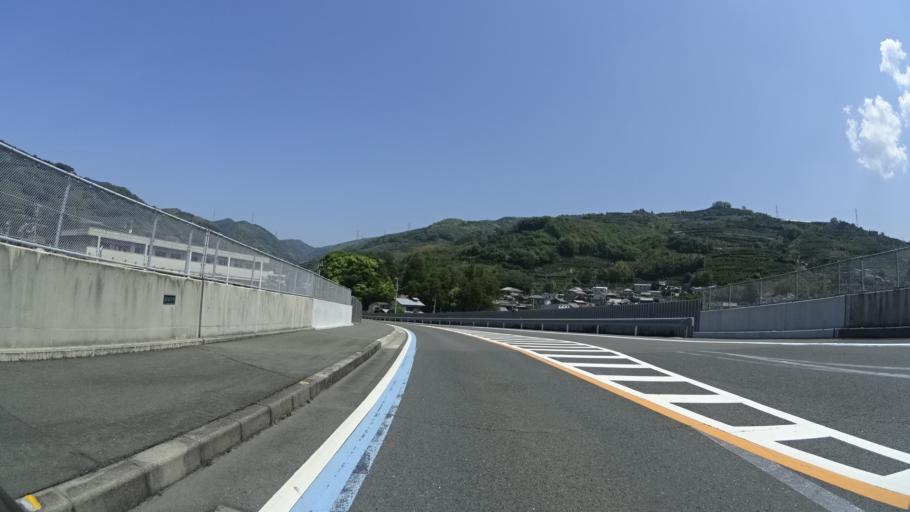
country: JP
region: Ehime
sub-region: Nishiuwa-gun
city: Ikata-cho
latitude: 33.4890
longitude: 132.3974
